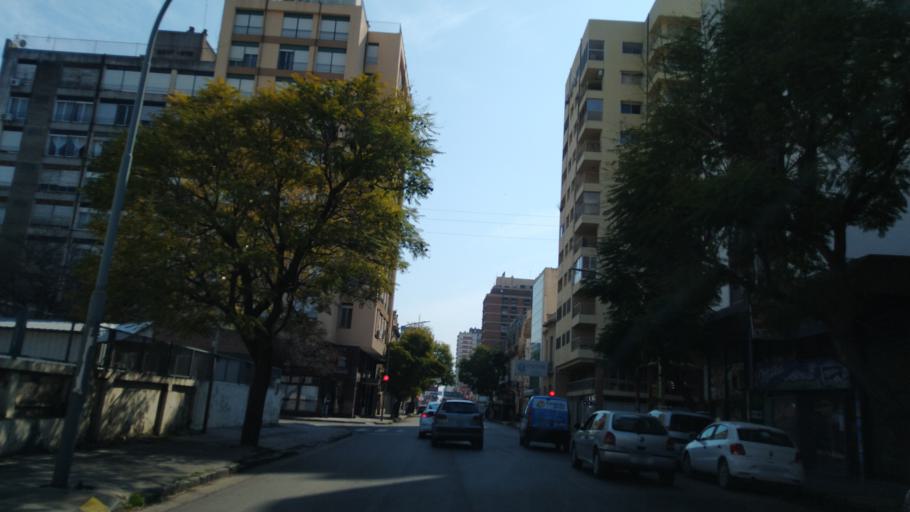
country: AR
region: Buenos Aires
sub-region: Partido de Bahia Blanca
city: Bahia Blanca
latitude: -38.7244
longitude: -62.2624
